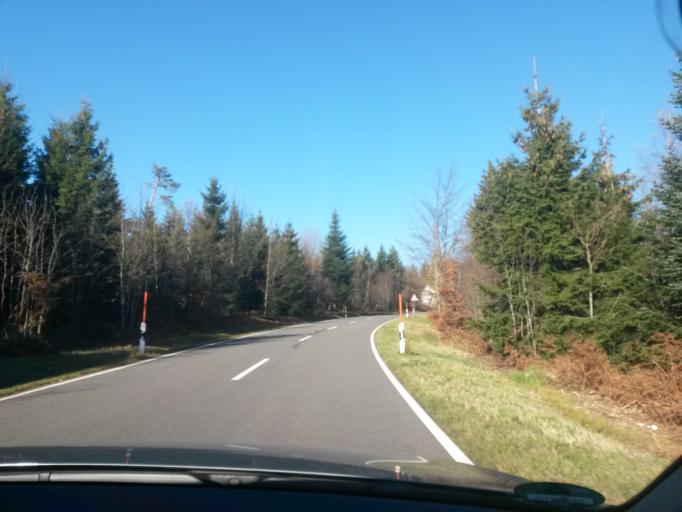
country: DE
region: Baden-Wuerttemberg
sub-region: Karlsruhe Region
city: Bad Rippoldsau-Schapbach
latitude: 48.4633
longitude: 8.2990
